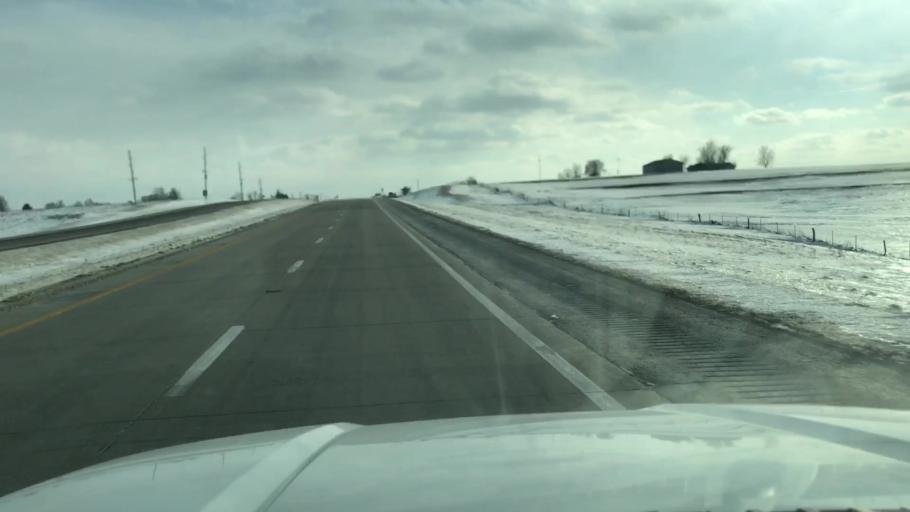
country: US
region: Missouri
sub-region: Nodaway County
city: Maryville
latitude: 40.2630
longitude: -94.8671
